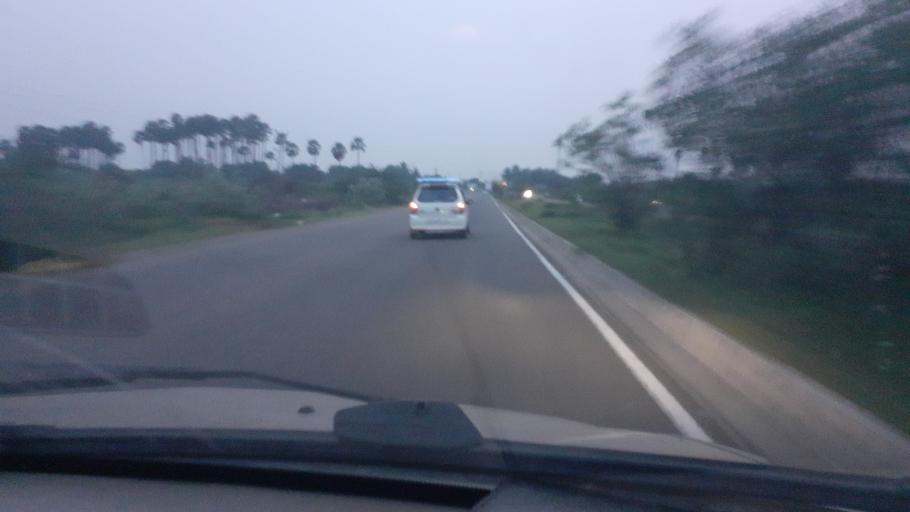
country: IN
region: Tamil Nadu
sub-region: Thoothukkudi
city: Srivaikuntam
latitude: 8.7117
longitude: 77.8265
